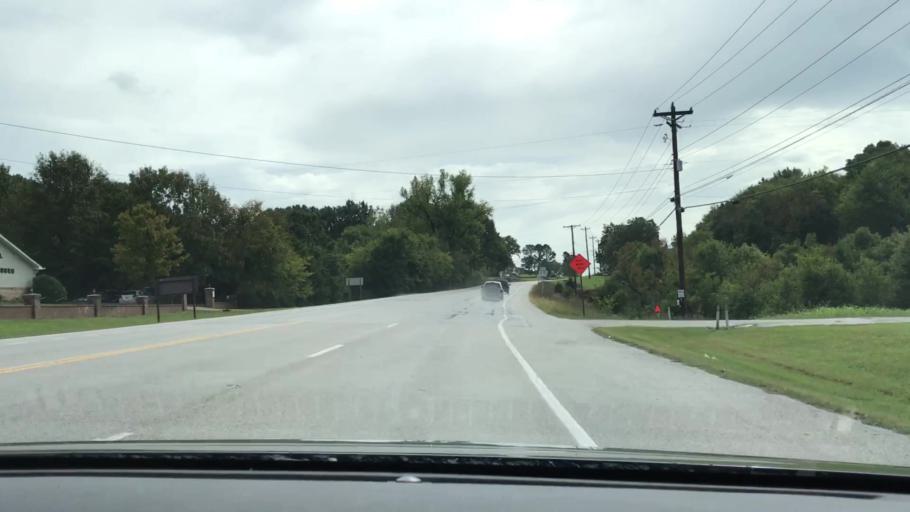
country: US
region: Tennessee
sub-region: Smith County
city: Carthage
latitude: 36.2868
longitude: -85.9914
